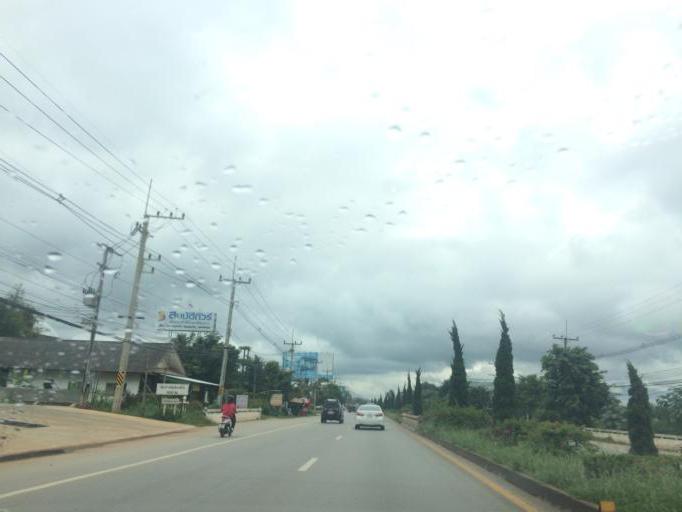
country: TH
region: Chiang Rai
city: Chiang Rai
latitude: 20.0107
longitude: 99.8684
